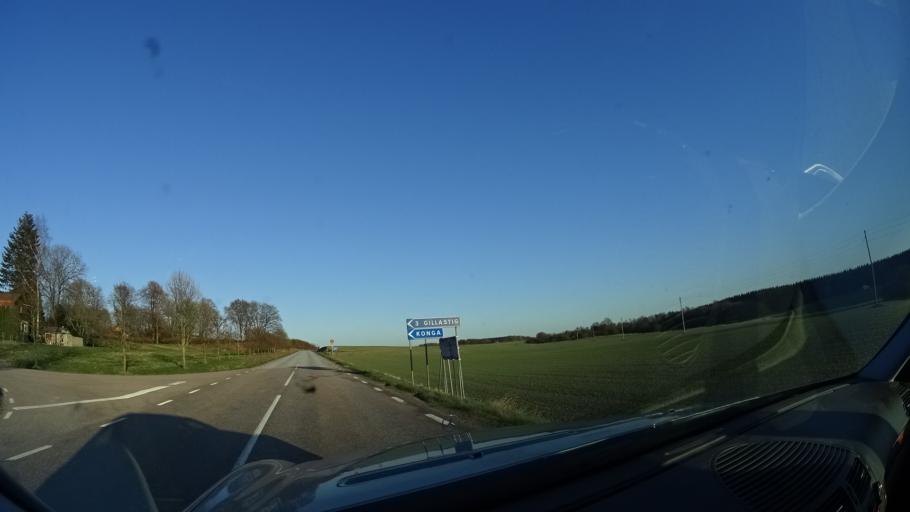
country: SE
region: Skane
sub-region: Klippans Kommun
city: Ljungbyhed
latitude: 55.9783
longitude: 13.1963
